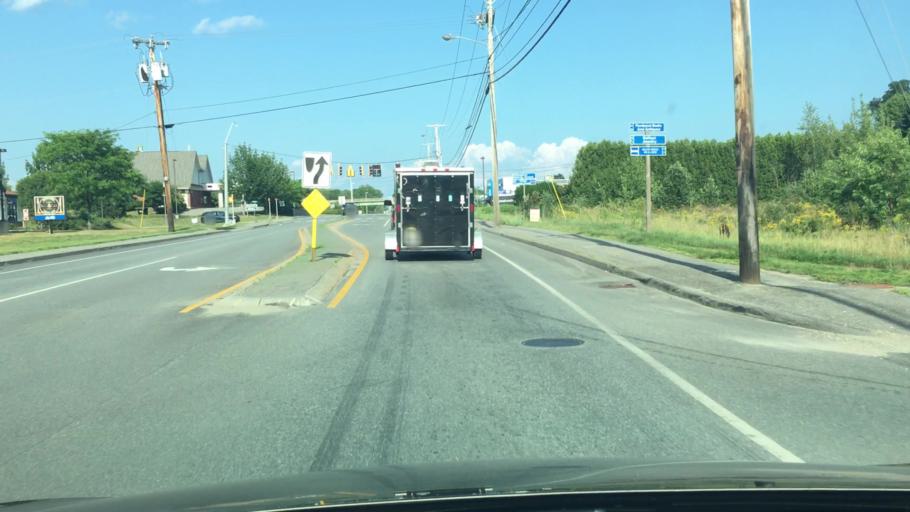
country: US
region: Maine
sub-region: Waldo County
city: Belfast
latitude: 44.4231
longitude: -69.0257
